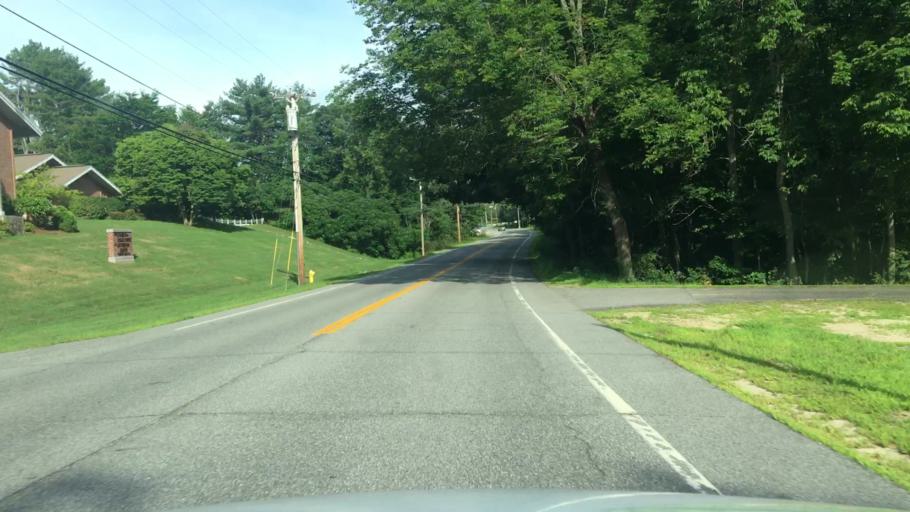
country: US
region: Maine
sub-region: Oxford County
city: Porter
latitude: 43.8046
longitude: -70.8694
